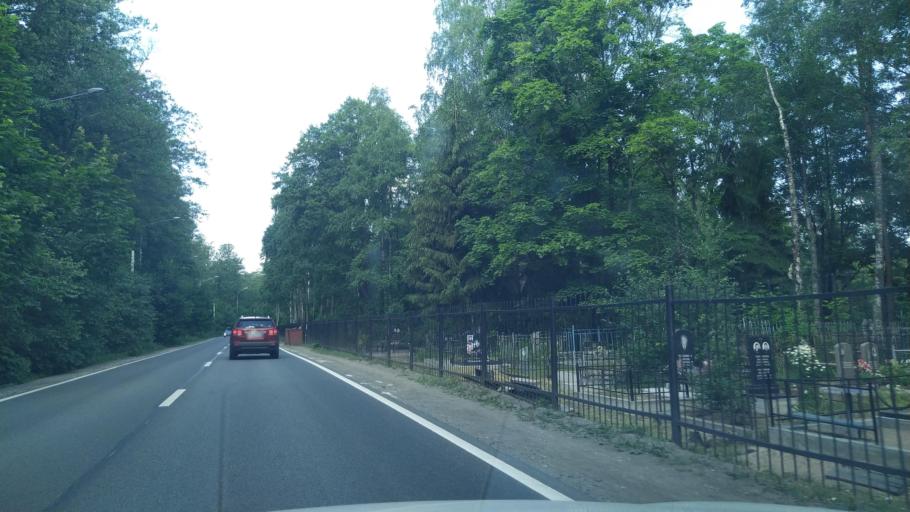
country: RU
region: St.-Petersburg
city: Kronshtadt
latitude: 60.0190
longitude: 29.7010
